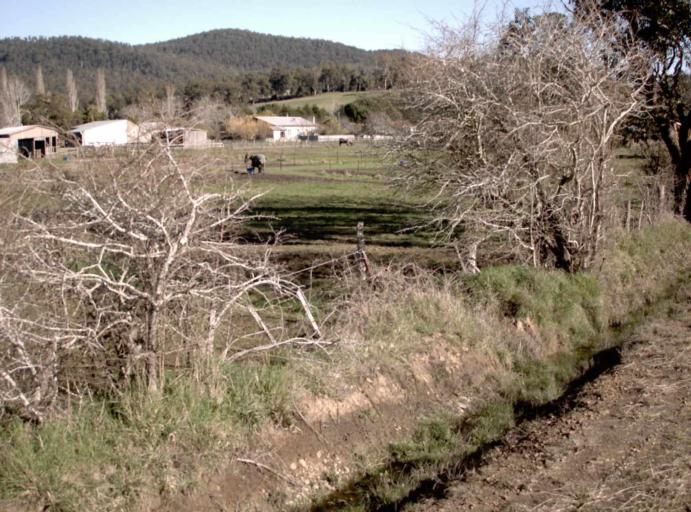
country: AU
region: Tasmania
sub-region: Launceston
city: Mayfield
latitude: -41.2545
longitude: 147.1548
